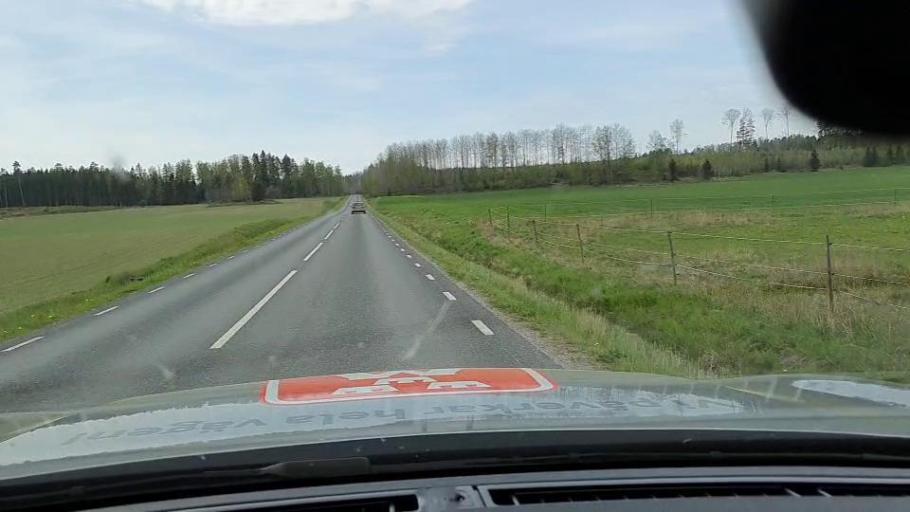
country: SE
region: Soedermanland
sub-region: Vingakers Kommun
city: Vingaker
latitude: 59.1191
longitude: 15.9483
